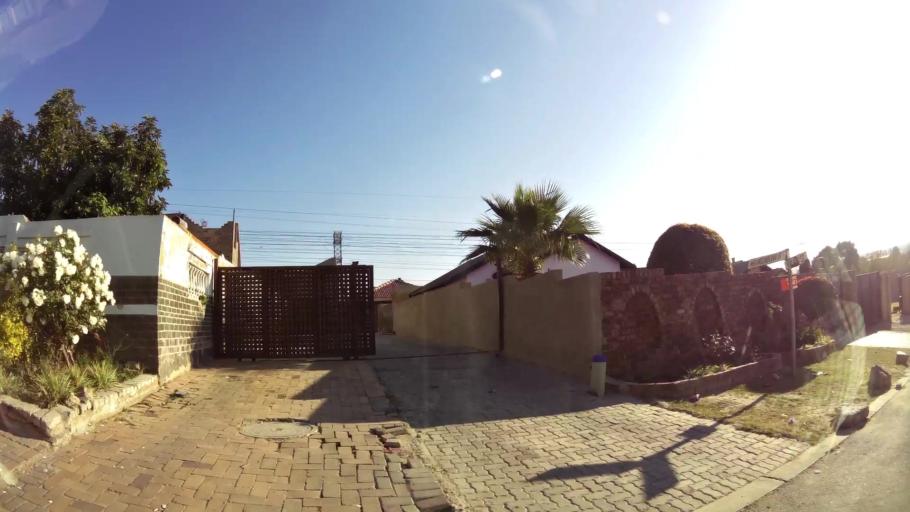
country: ZA
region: Gauteng
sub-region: City of Johannesburg Metropolitan Municipality
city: Modderfontein
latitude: -26.0419
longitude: 28.1533
